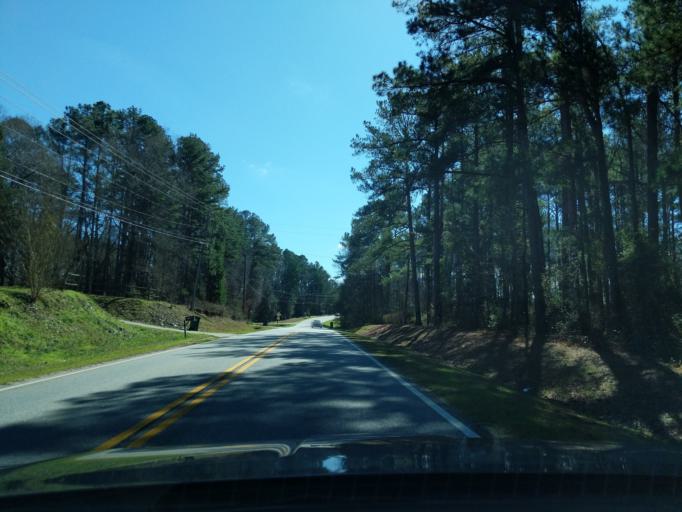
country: US
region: Georgia
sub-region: Columbia County
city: Evans
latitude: 33.5439
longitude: -82.1654
